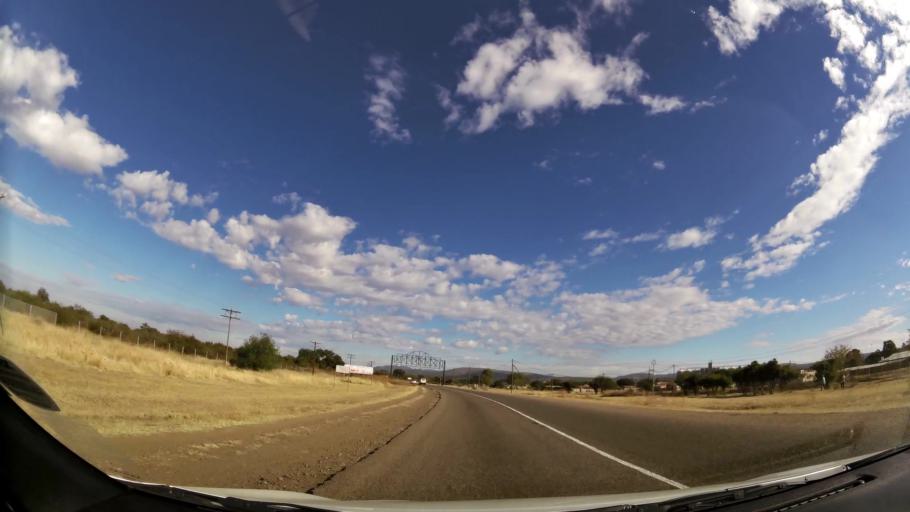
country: ZA
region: Limpopo
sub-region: Waterberg District Municipality
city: Bela-Bela
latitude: -24.8918
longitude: 28.3083
